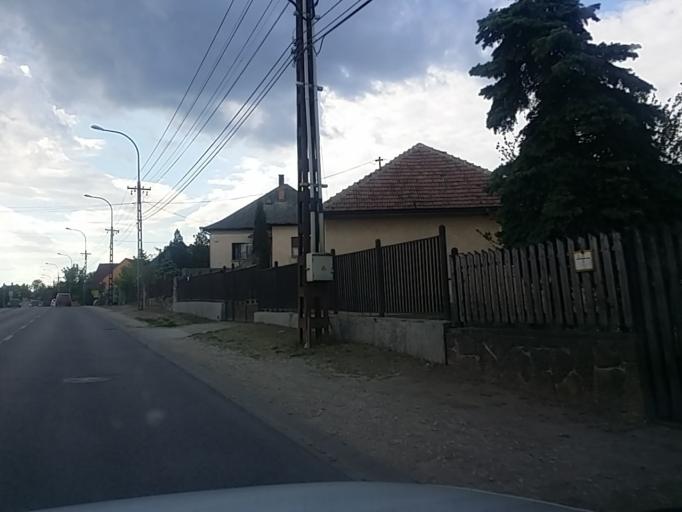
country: HU
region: Pest
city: Veresegyhaz
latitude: 47.6542
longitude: 19.2773
